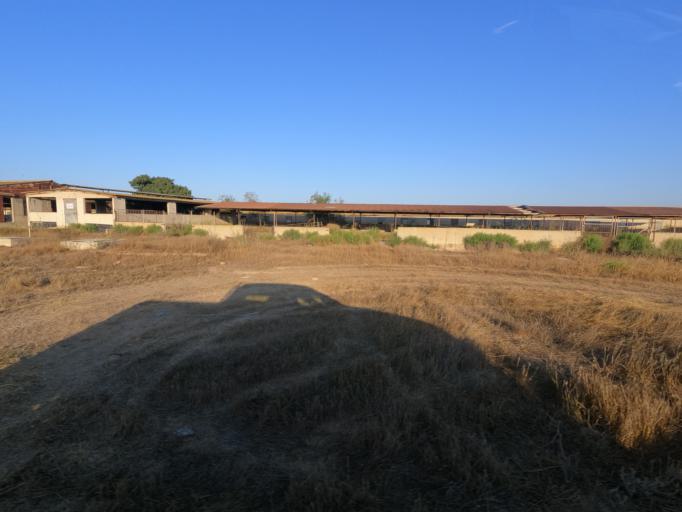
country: CY
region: Ammochostos
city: Avgorou
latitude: 35.0131
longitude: 33.8030
